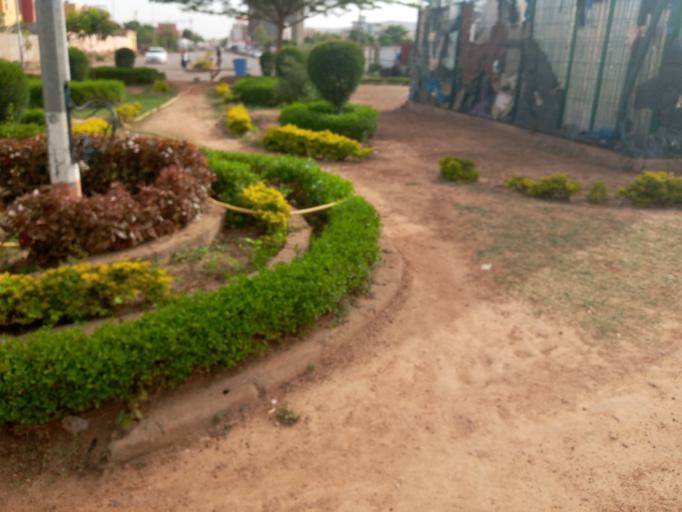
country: ML
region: Bamako
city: Bamako
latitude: 12.6302
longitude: -8.0273
